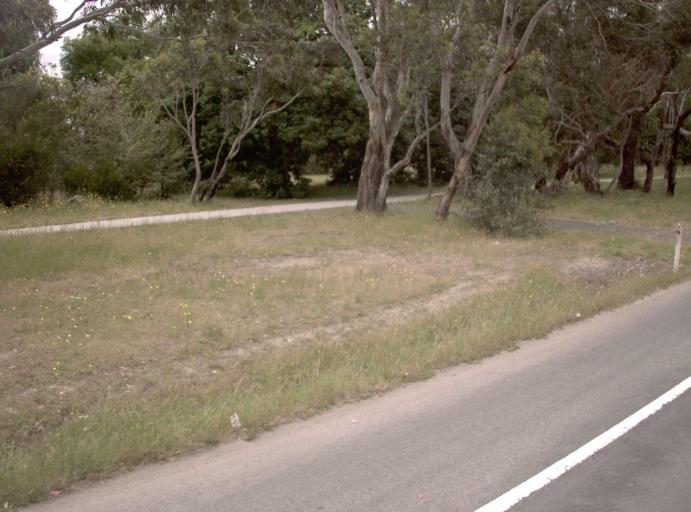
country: AU
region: Victoria
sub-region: Casey
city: Hampton Park
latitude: -38.0395
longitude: 145.2502
